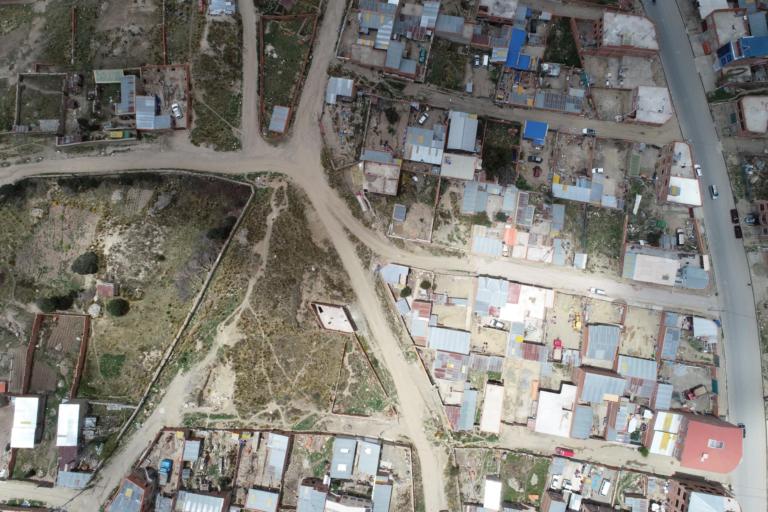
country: BO
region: La Paz
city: La Paz
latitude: -16.4433
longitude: -68.1438
